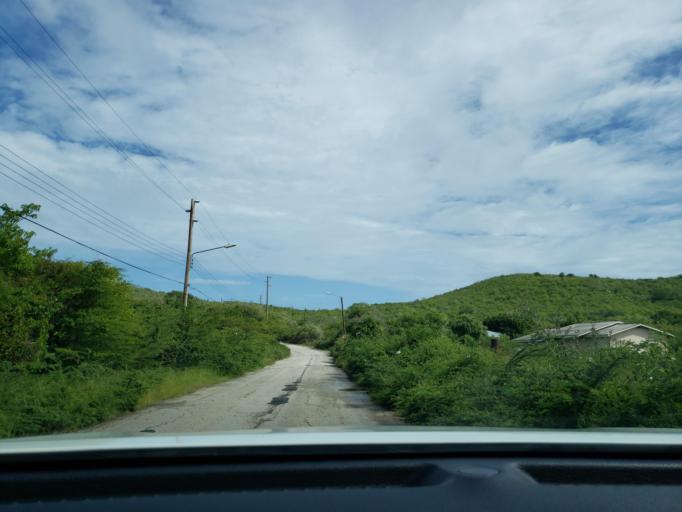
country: CW
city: Barber
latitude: 12.3065
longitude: -69.0901
